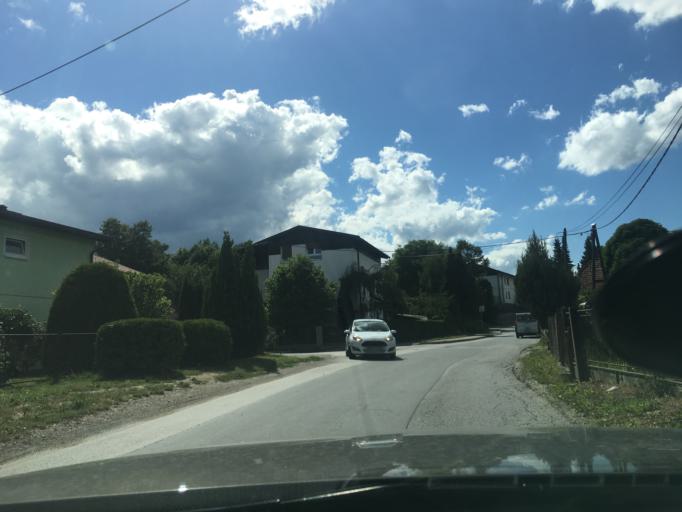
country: SI
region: Maribor
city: Pekre
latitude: 46.5473
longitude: 15.5970
